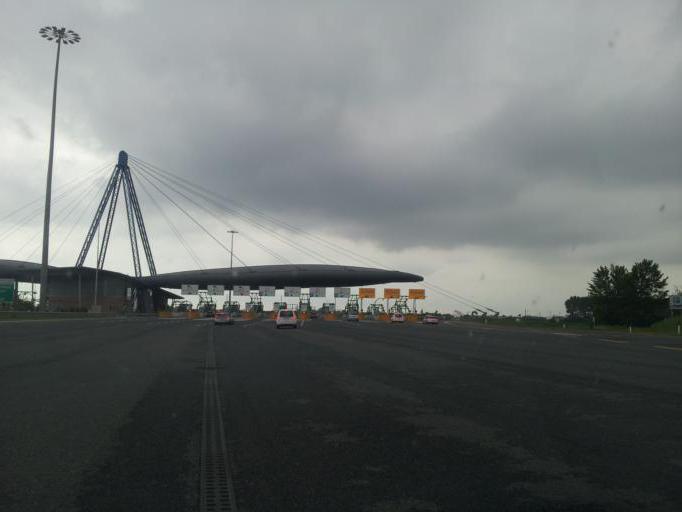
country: IT
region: Friuli Venezia Giulia
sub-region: Provincia di Udine
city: Ronchis
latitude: 45.8081
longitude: 13.0208
